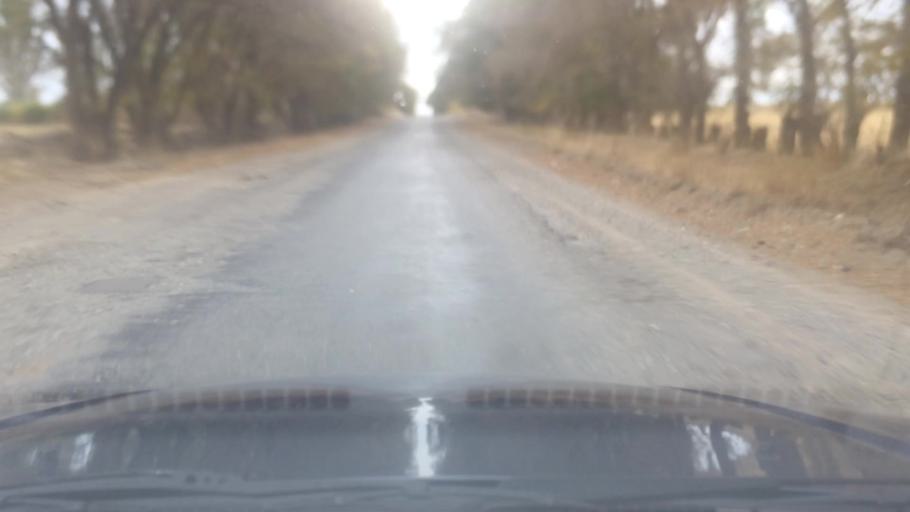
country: KG
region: Ysyk-Koel
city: Balykchy
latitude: 42.3033
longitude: 76.4787
